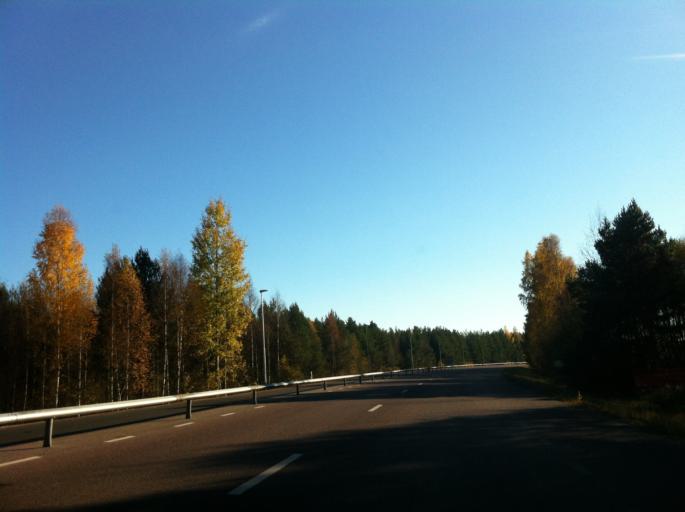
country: SE
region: Dalarna
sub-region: Mora Kommun
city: Mora
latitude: 61.0237
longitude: 14.5348
